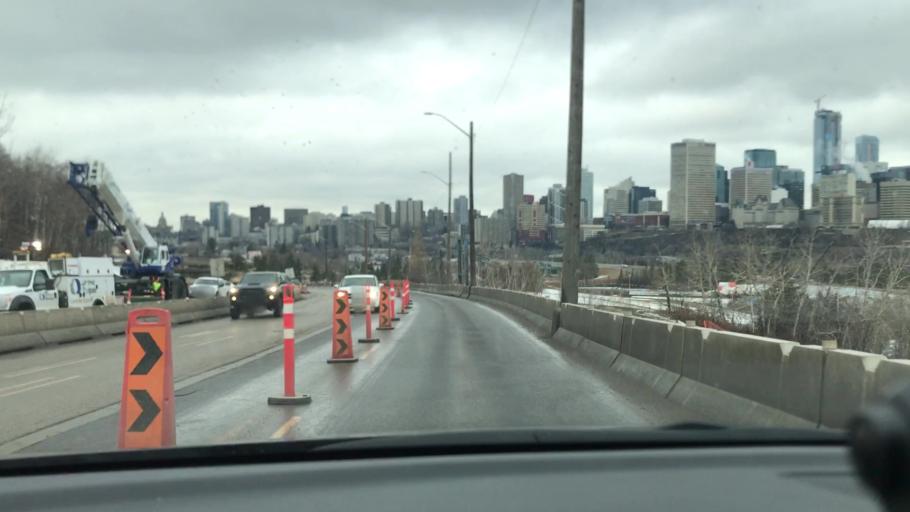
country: CA
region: Alberta
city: Edmonton
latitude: 53.5329
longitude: -113.4746
